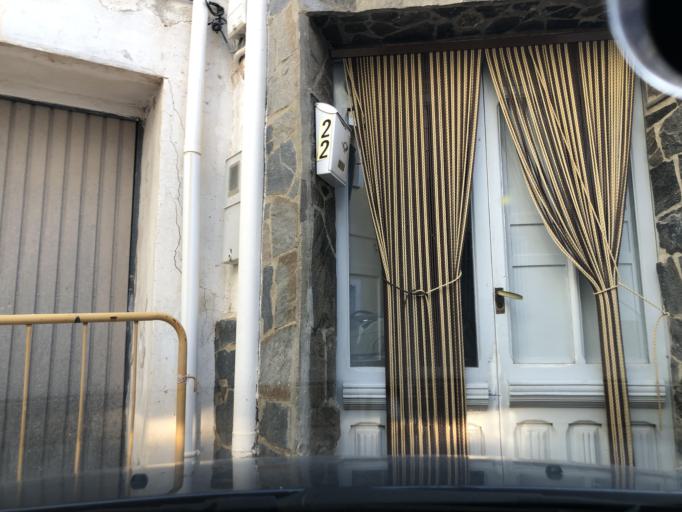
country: ES
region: Valencia
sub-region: Provincia de Alicante
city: Callosa d'En Sarria
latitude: 38.6515
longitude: -0.1236
